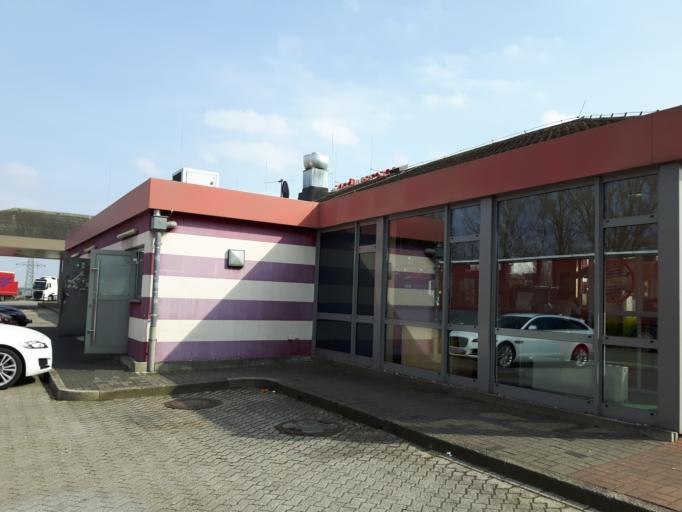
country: DE
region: North Rhine-Westphalia
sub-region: Regierungsbezirk Arnsberg
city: Soest
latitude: 51.5486
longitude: 8.1330
